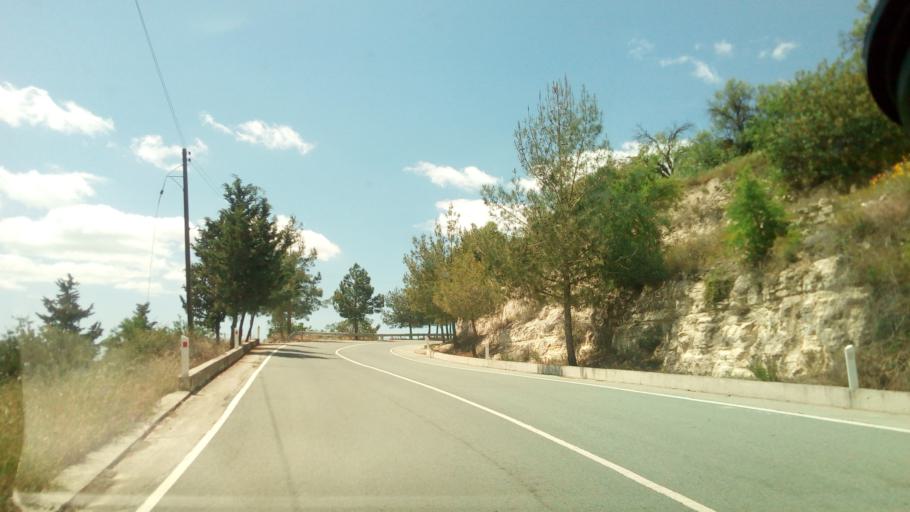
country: CY
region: Limassol
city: Pachna
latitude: 34.8398
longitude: 32.7723
